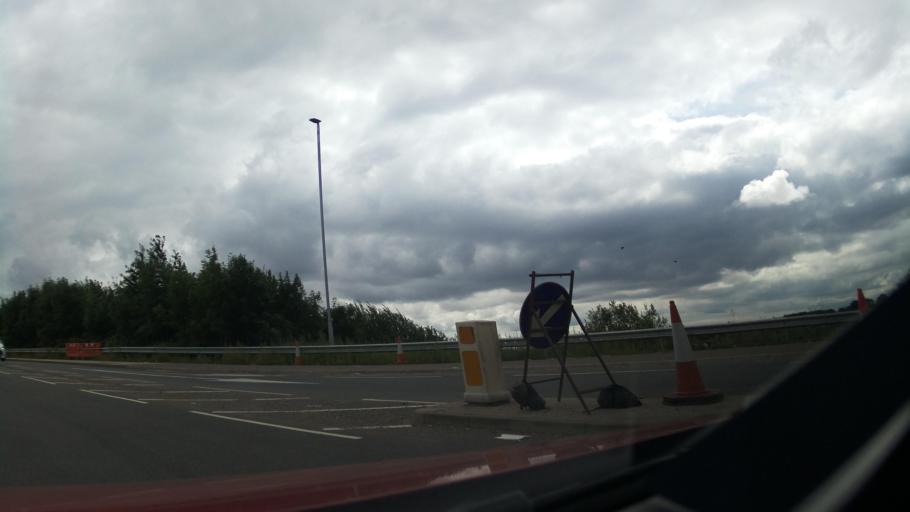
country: GB
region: England
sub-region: Nottinghamshire
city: Burton Joyce
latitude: 52.9759
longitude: -1.0598
